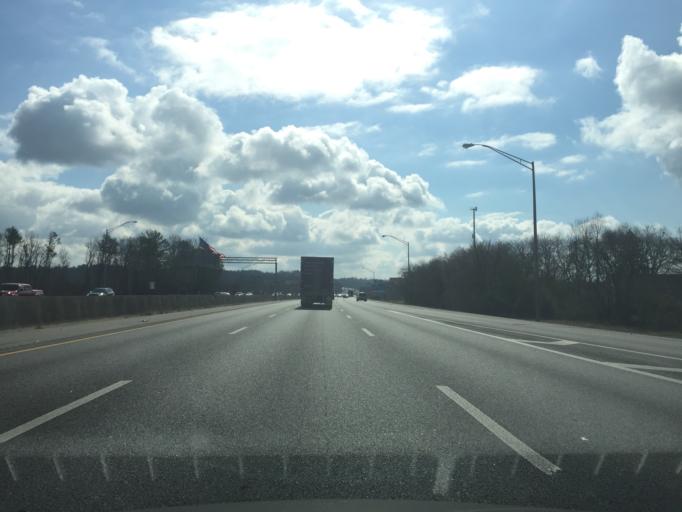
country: US
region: Georgia
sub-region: Catoosa County
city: Indian Springs
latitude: 34.9881
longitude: -85.2028
